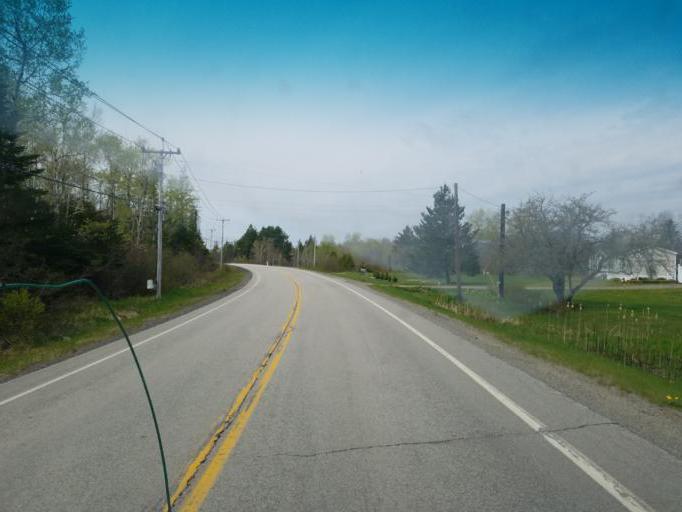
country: US
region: Maine
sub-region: Washington County
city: Eastport
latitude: 44.8016
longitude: -67.1375
